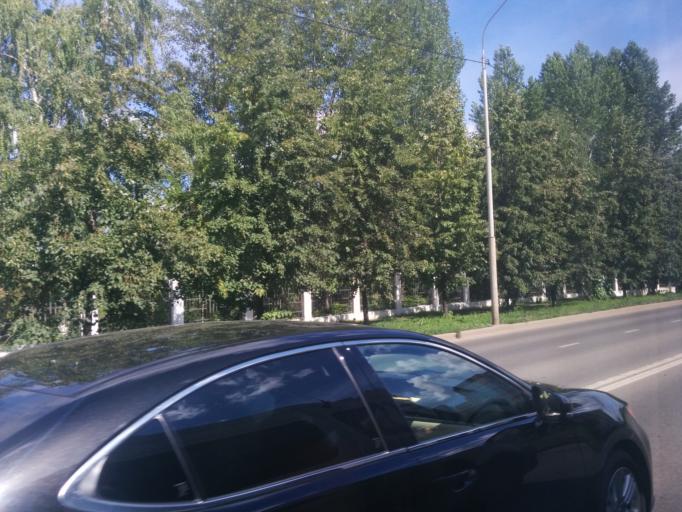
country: RU
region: Tatarstan
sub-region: Gorod Kazan'
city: Kazan
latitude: 55.7967
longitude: 49.1942
